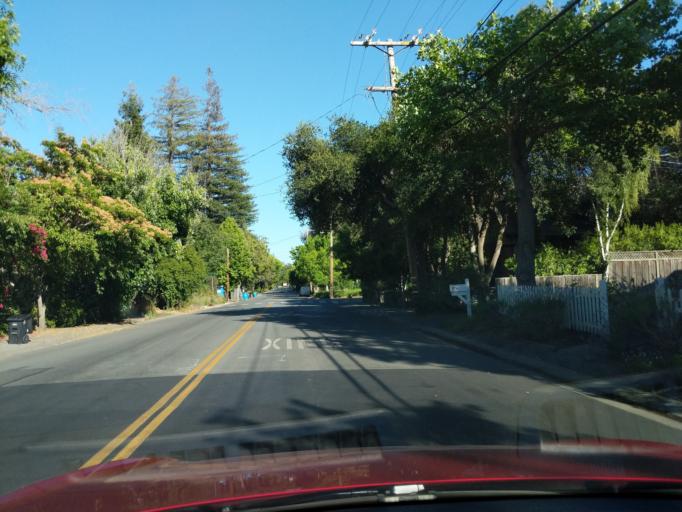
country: US
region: California
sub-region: San Mateo County
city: West Menlo Park
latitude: 37.4382
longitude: -122.1898
